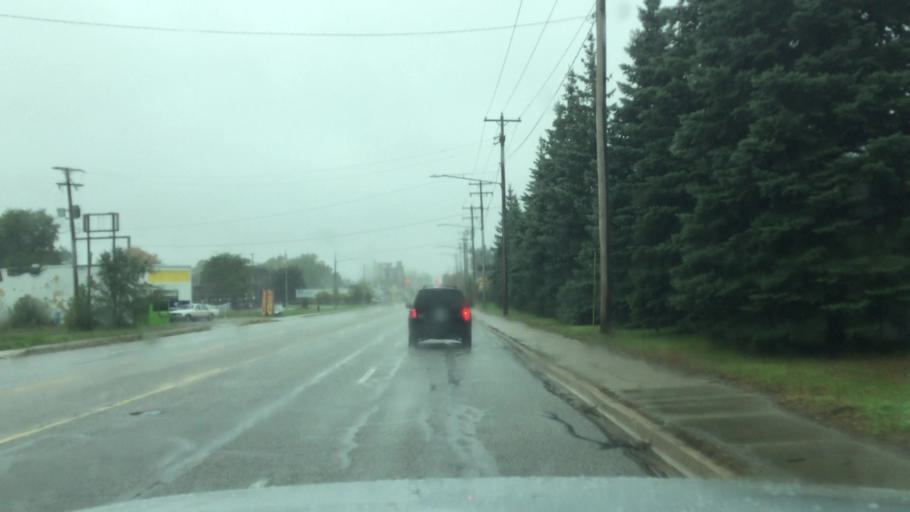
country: US
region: Michigan
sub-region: Saginaw County
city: Buena Vista
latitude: 43.4126
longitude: -83.9201
